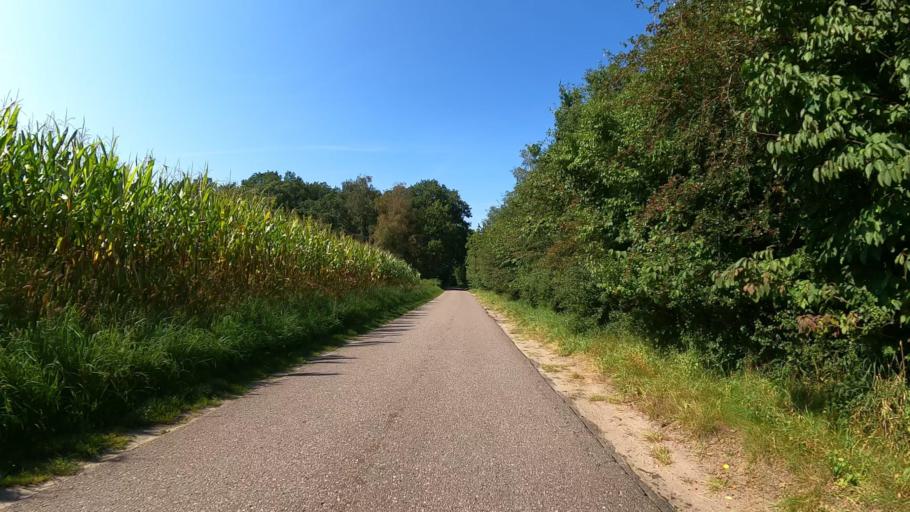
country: DE
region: Schleswig-Holstein
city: Nutzen
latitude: 53.8692
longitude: 9.9045
